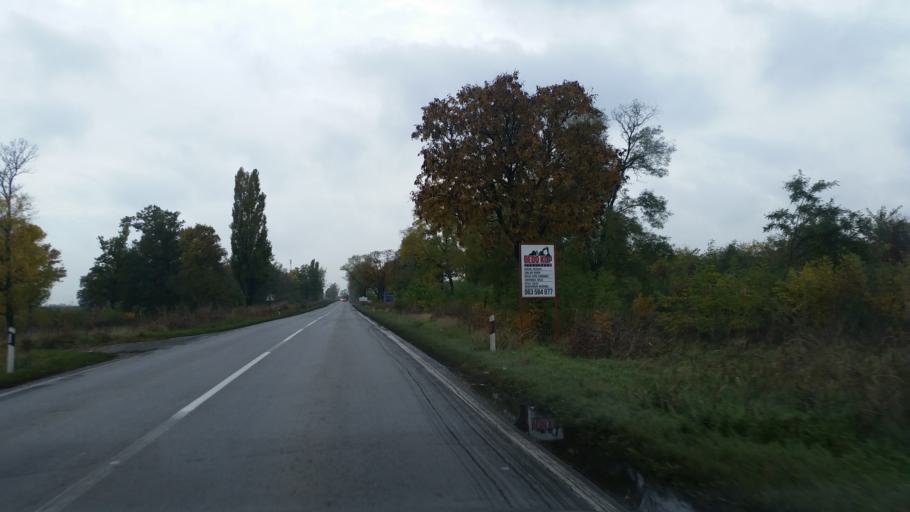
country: RS
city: Ecka
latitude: 45.3341
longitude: 20.4361
